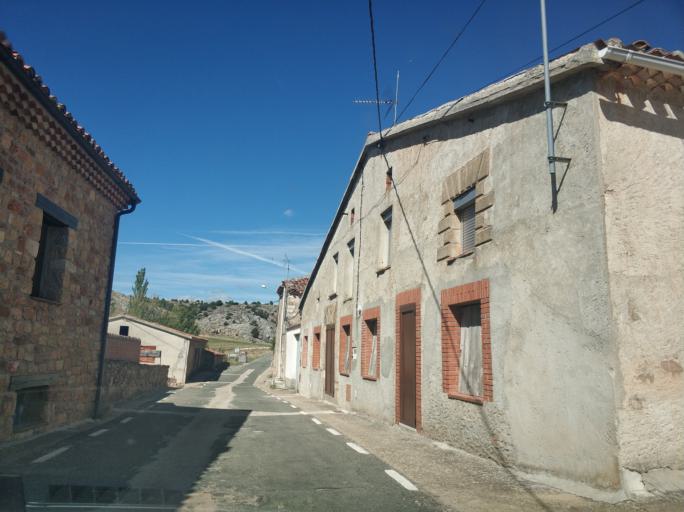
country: ES
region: Castille and Leon
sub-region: Provincia de Soria
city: Espeja de San Marcelino
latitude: 41.8032
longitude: -3.2226
